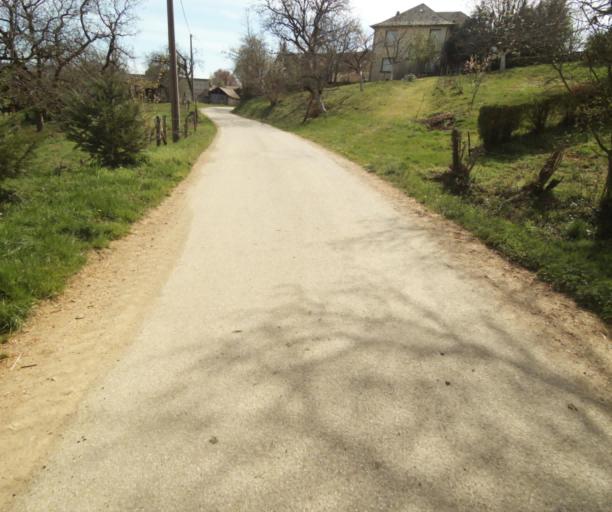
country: FR
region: Limousin
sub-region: Departement de la Correze
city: Naves
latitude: 45.3508
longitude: 1.7982
